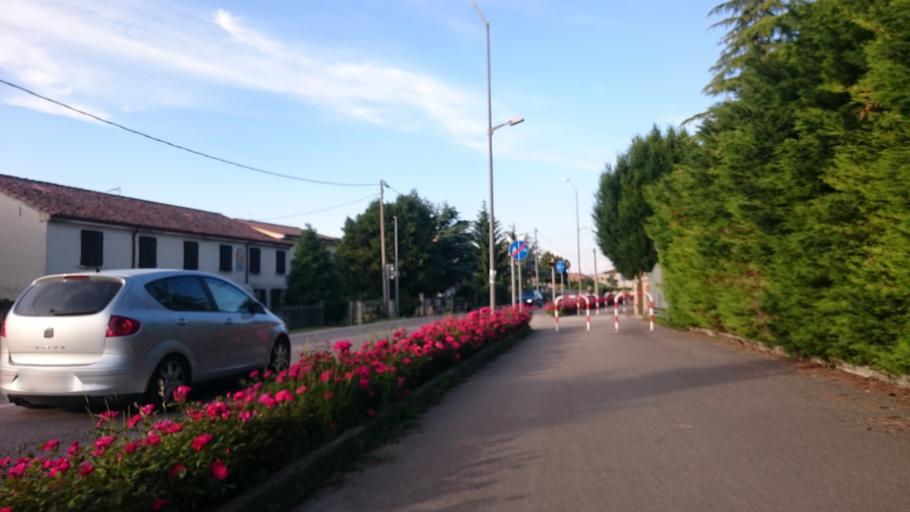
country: IT
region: Veneto
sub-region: Provincia di Verona
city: Roncanova
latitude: 45.1470
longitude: 11.1123
